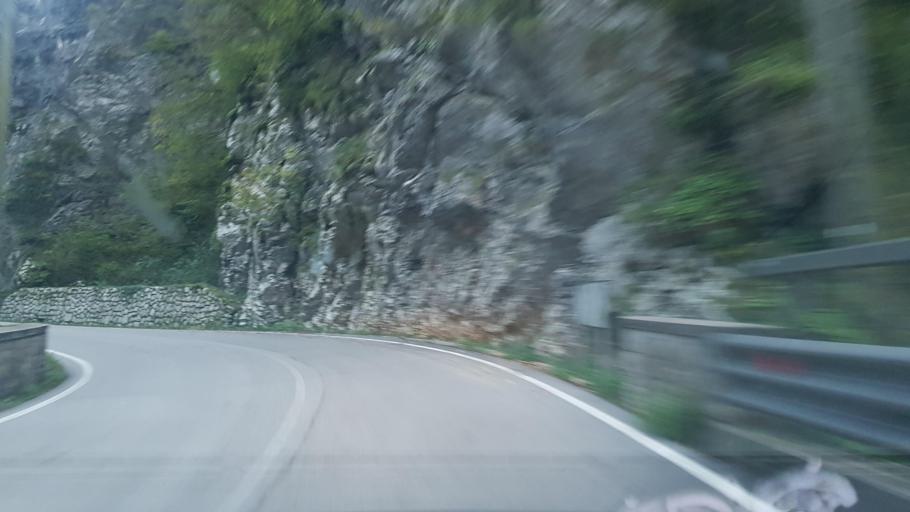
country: IT
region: Friuli Venezia Giulia
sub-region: Provincia di Pordenone
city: Anduins
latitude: 46.2695
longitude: 12.9537
